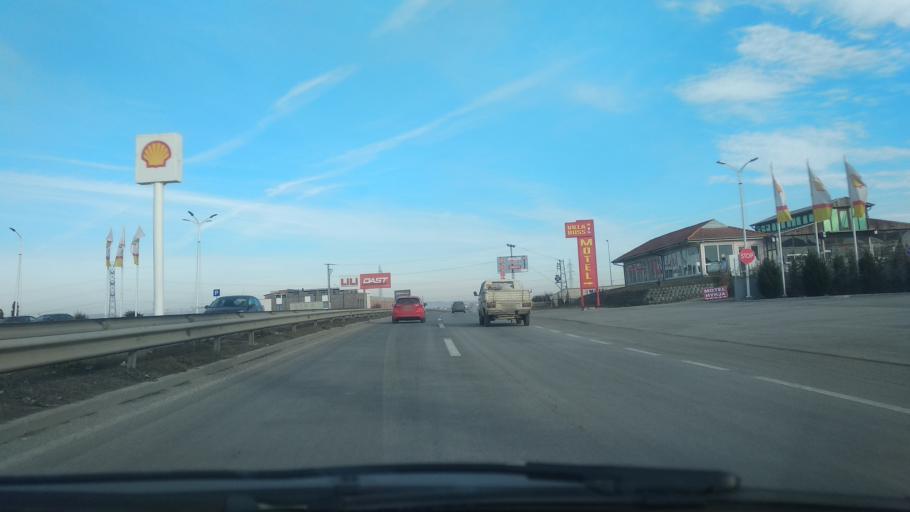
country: XK
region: Pristina
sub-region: Kosovo Polje
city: Kosovo Polje
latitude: 42.6770
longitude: 21.1153
